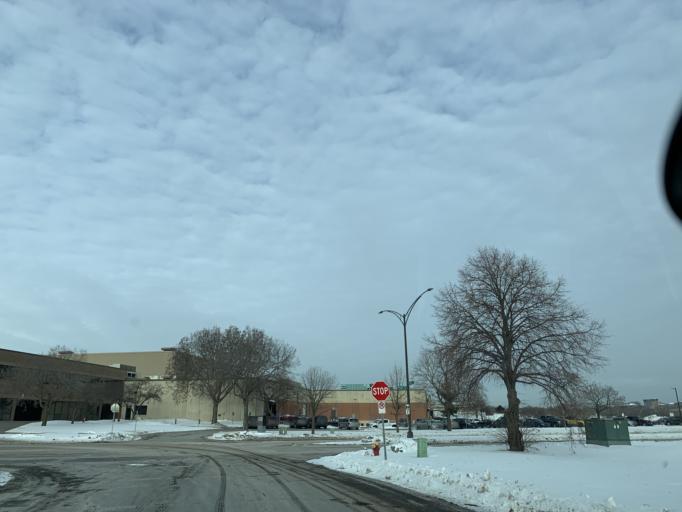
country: US
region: Minnesota
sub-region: Ramsey County
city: Saint Paul
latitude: 44.9408
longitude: -93.0727
